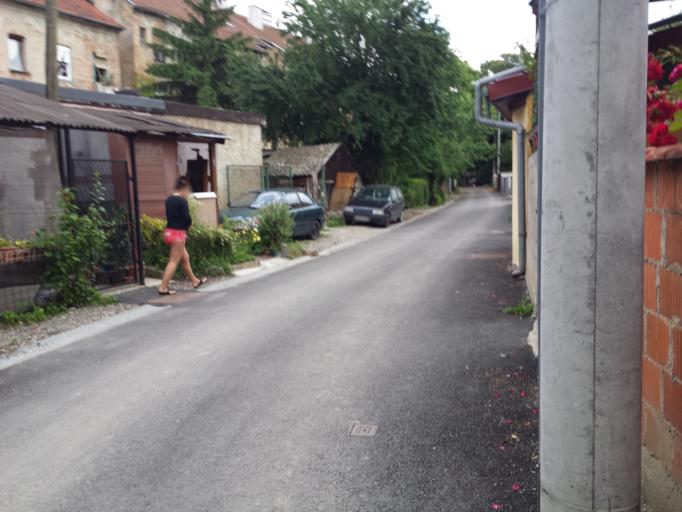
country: HR
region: Grad Zagreb
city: Novi Zagreb
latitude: 45.7980
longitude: 15.9799
